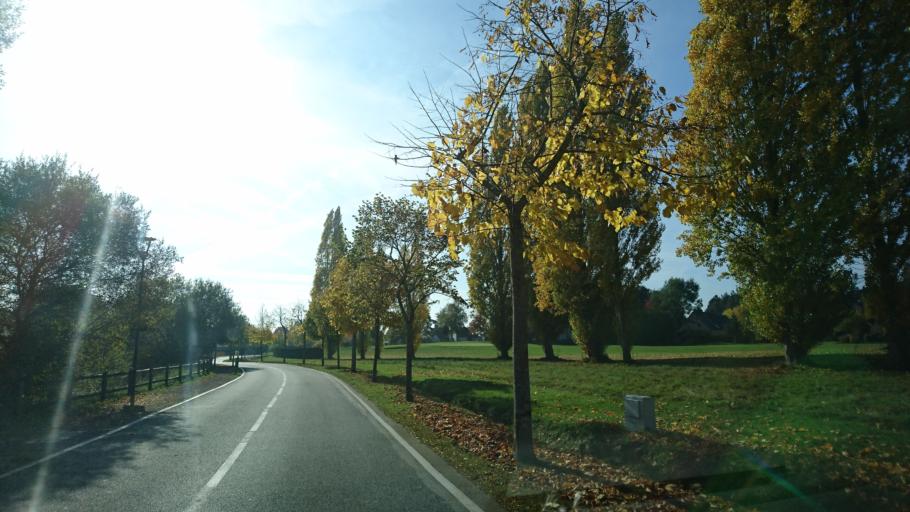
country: FR
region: Brittany
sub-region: Departement d'Ille-et-Vilaine
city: Bruz
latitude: 48.0356
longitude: -1.7656
